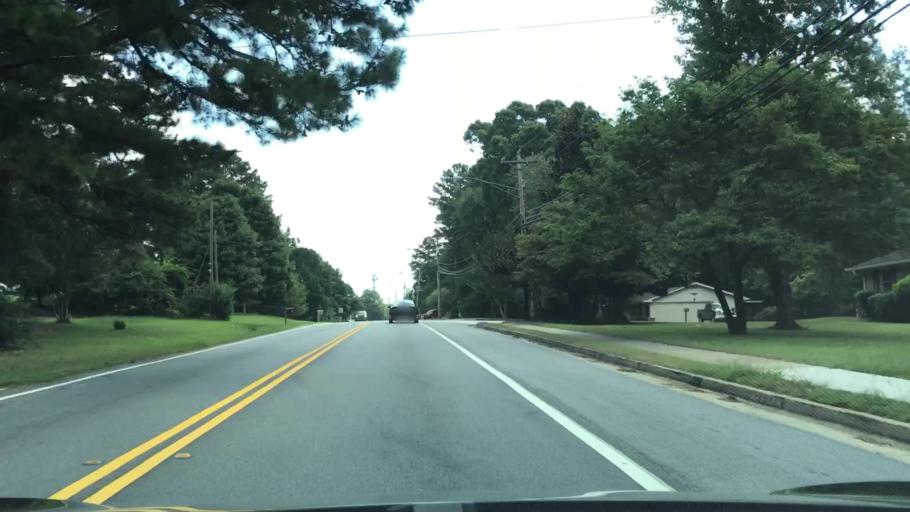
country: US
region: Georgia
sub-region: Gwinnett County
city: Snellville
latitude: 33.8911
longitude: -84.0658
